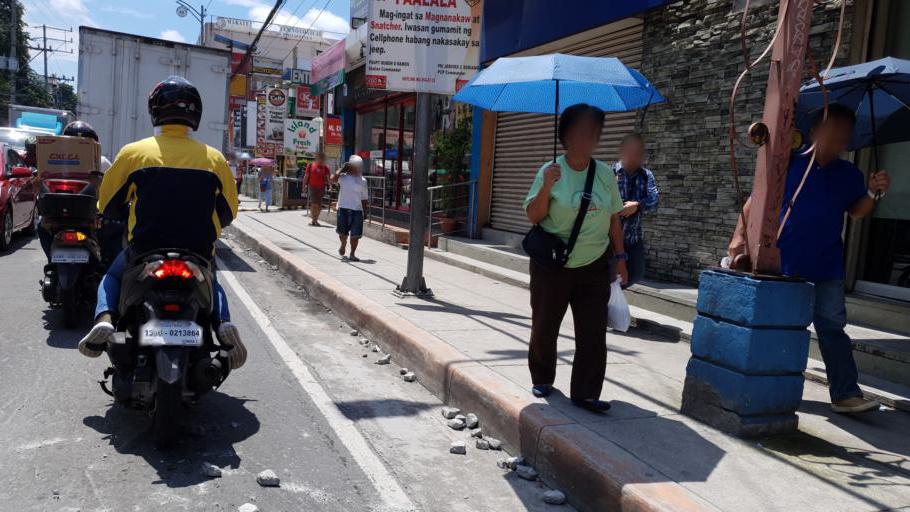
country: PH
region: Metro Manila
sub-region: San Juan
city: San Juan
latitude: 14.6017
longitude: 121.0123
